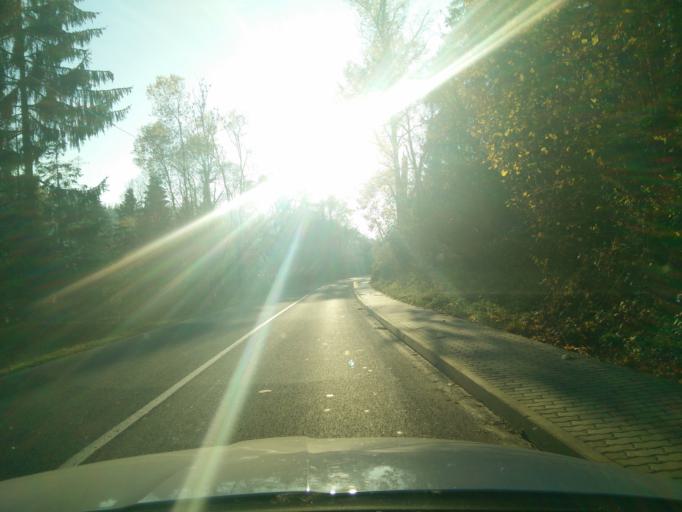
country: PL
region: Silesian Voivodeship
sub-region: Powiat zywiecki
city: Rycerka Gorna
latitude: 49.3615
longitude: 19.0485
